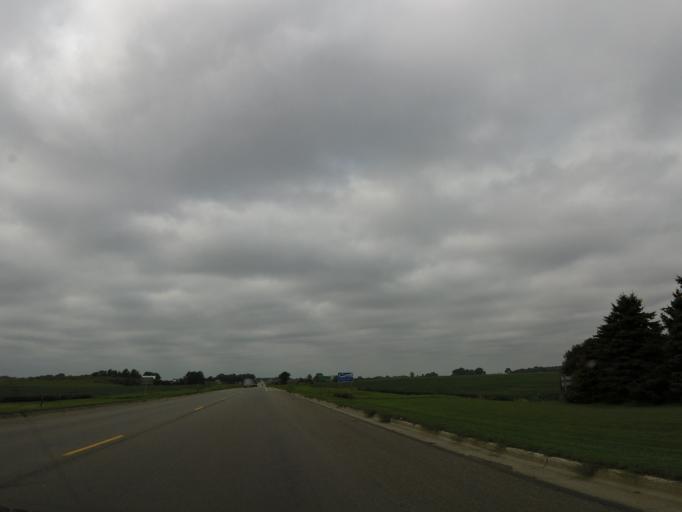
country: US
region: Minnesota
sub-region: Renville County
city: Renville
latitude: 44.7889
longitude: -95.1070
